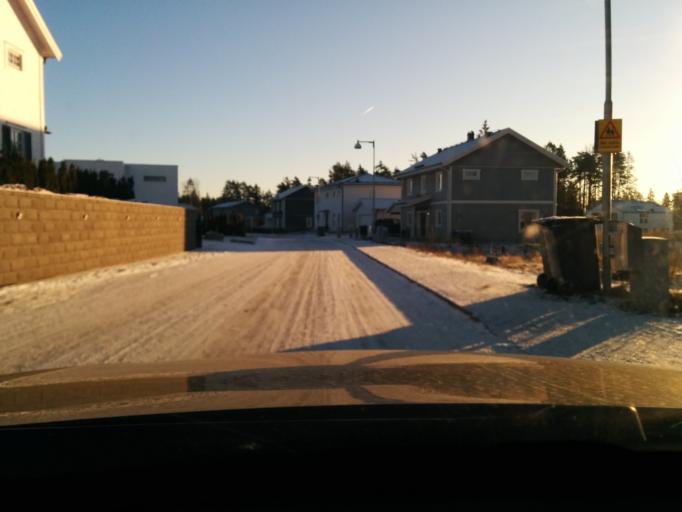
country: SE
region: Stockholm
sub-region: Vallentuna Kommun
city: Vallentuna
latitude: 59.5041
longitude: 18.0827
